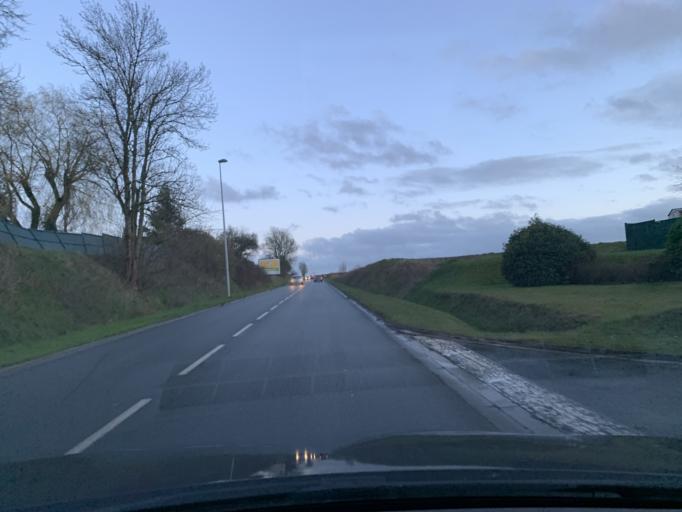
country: FR
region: Nord-Pas-de-Calais
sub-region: Departement du Nord
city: Cambrai
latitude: 50.1552
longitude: 3.2599
